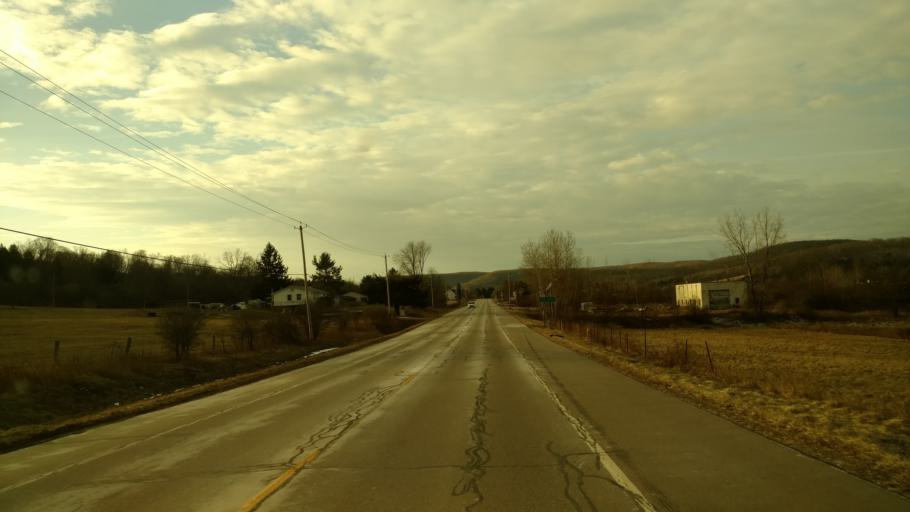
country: US
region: New York
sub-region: Allegany County
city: Wellsville
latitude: 42.0542
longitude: -77.9159
